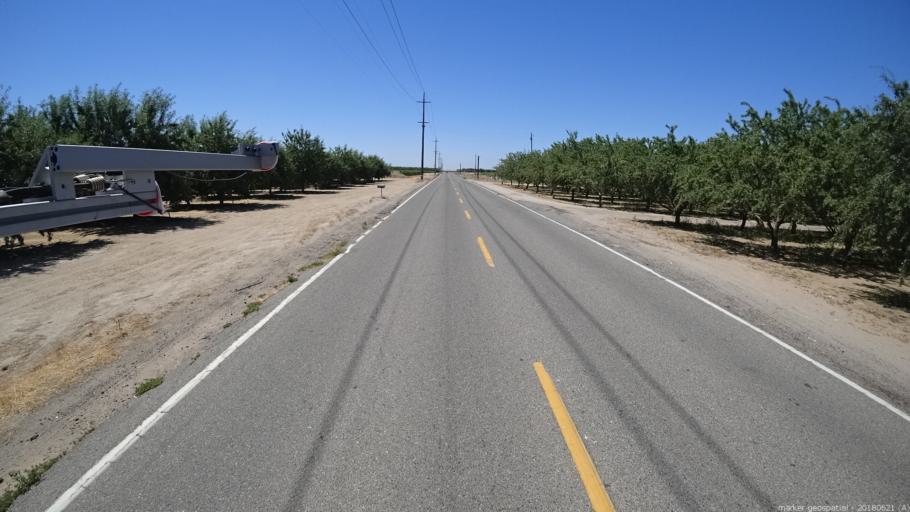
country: US
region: California
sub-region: Madera County
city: Bonadelle Ranchos-Madera Ranchos
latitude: 36.8702
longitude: -119.9113
